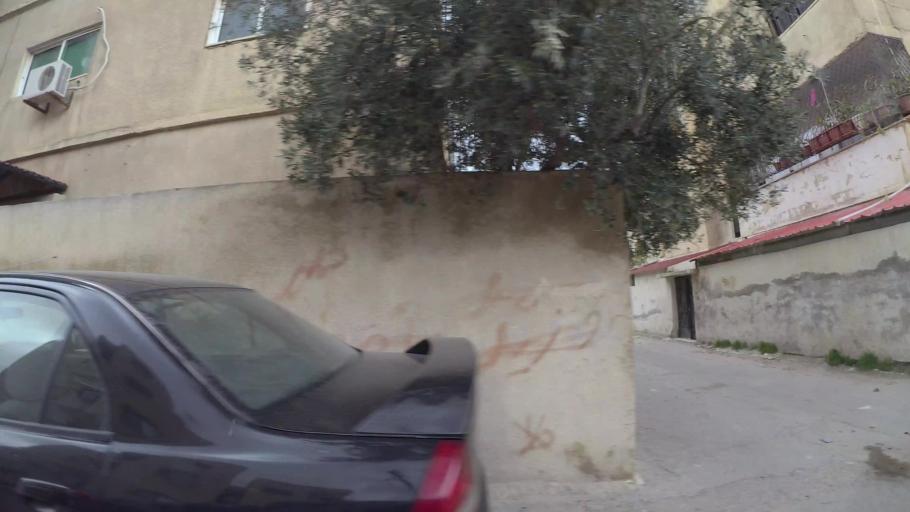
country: JO
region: Amman
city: Amman
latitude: 32.0096
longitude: 35.9484
